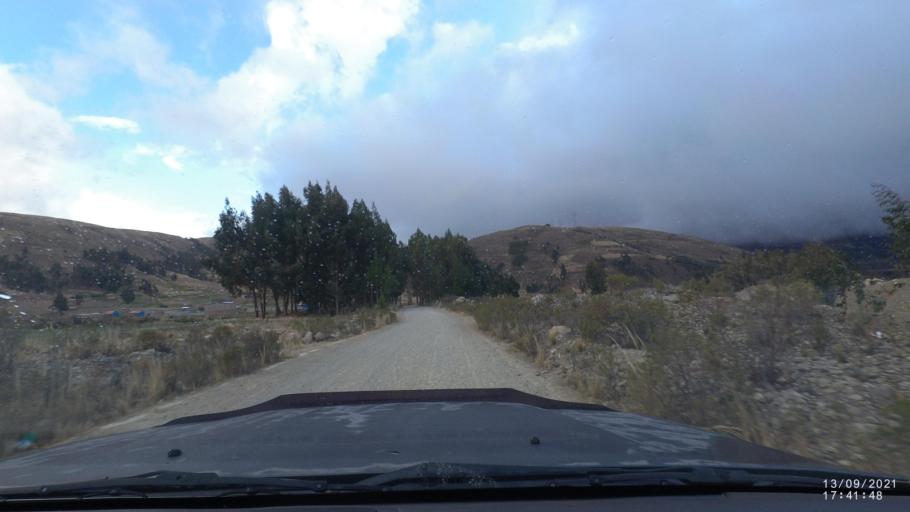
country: BO
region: Cochabamba
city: Colomi
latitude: -17.3661
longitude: -65.8140
